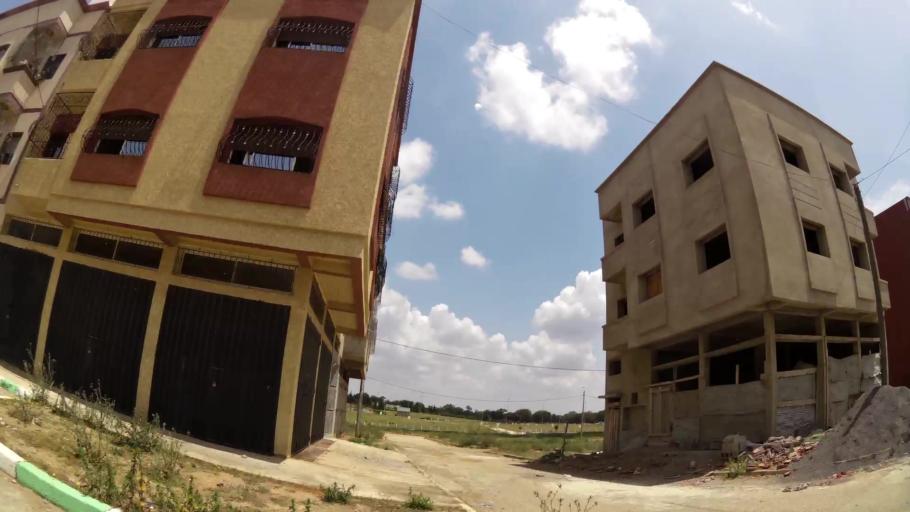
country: MA
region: Rabat-Sale-Zemmour-Zaer
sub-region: Khemisset
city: Tiflet
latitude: 34.0130
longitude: -6.5207
